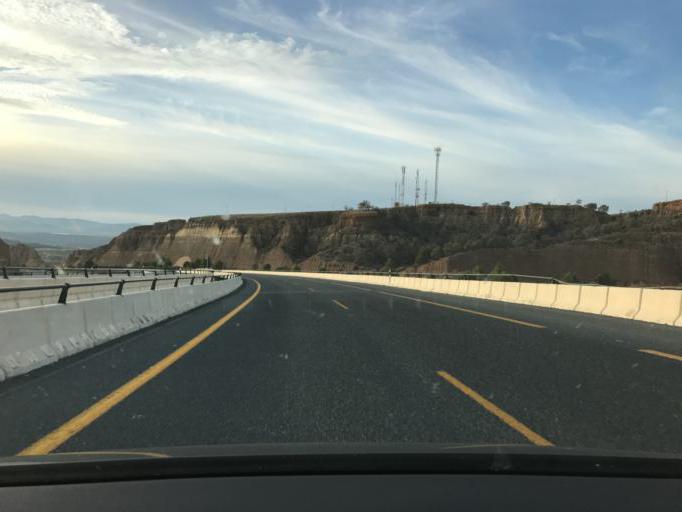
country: ES
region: Andalusia
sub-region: Provincia de Granada
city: Guadix
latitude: 37.3201
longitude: -3.1158
